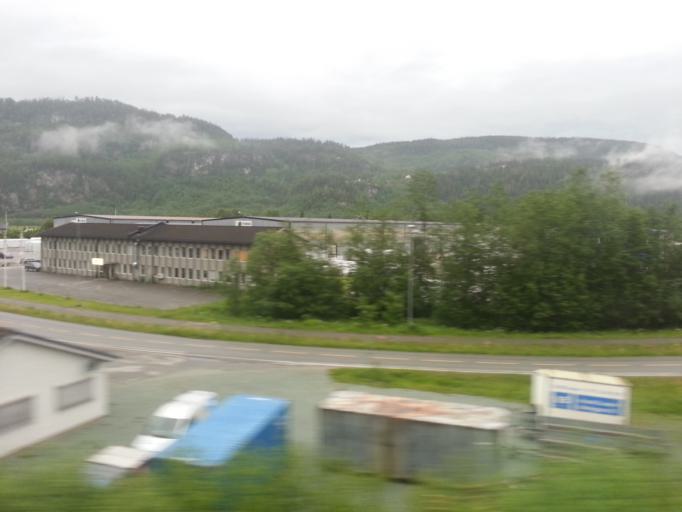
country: NO
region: Sor-Trondelag
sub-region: Midtre Gauldal
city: Storen
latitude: 63.0445
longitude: 10.2816
